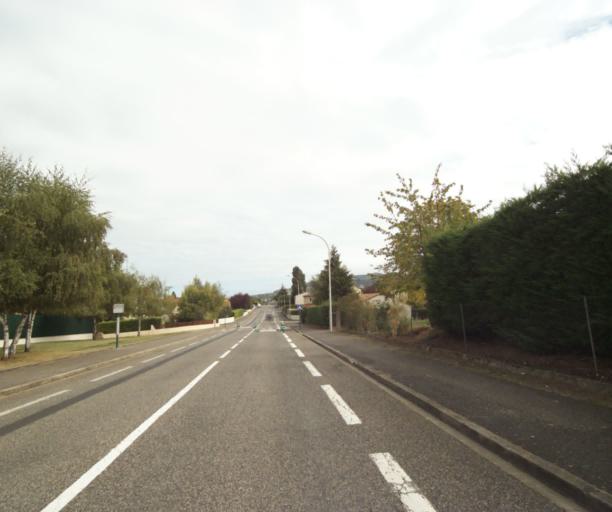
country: FR
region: Auvergne
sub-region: Departement du Puy-de-Dome
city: Le Cendre
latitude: 45.7177
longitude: 3.1912
